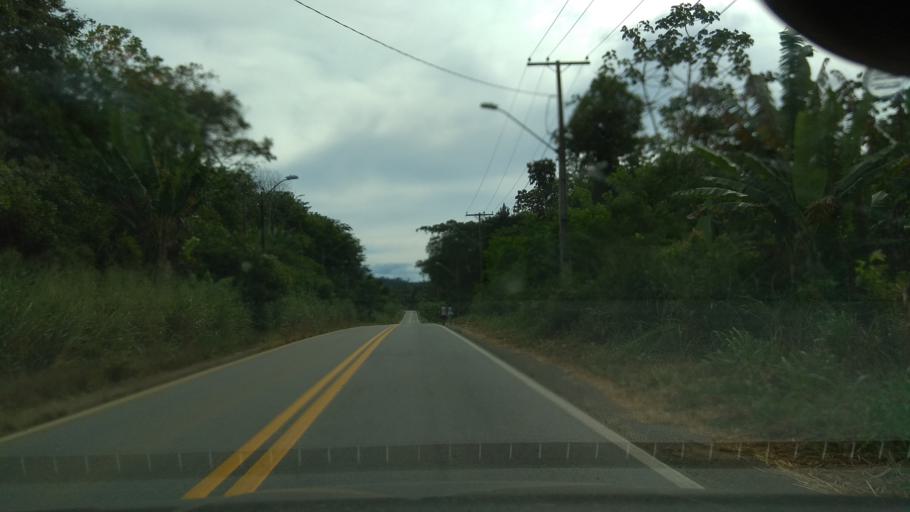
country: BR
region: Bahia
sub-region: Ubata
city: Ubata
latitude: -14.1963
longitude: -39.5436
